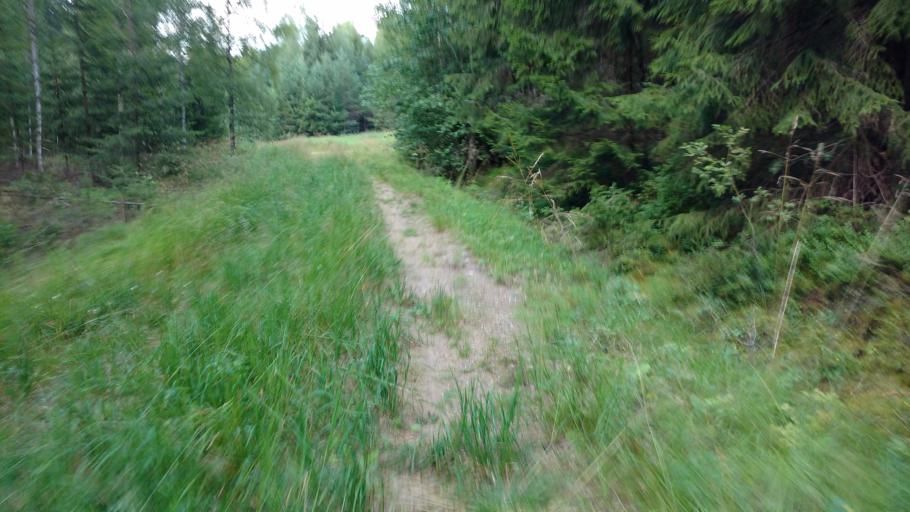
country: FI
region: Varsinais-Suomi
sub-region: Salo
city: Pertteli
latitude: 60.3932
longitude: 23.2282
